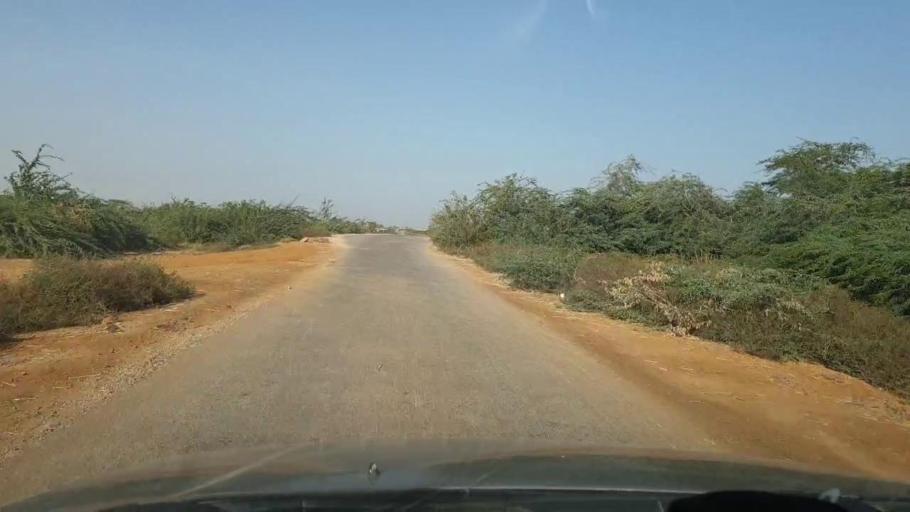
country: PK
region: Sindh
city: Bulri
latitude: 25.0957
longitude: 68.2353
